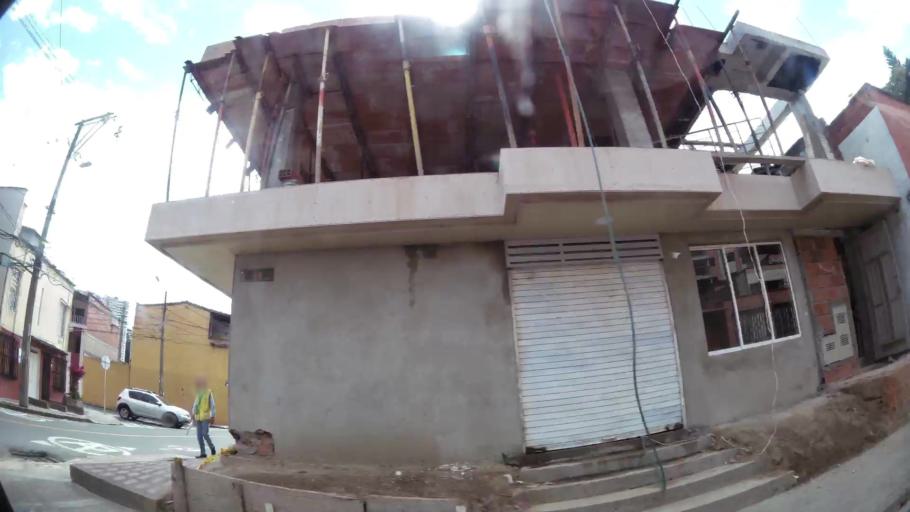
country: CO
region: Antioquia
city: Sabaneta
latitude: 6.1541
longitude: -75.6116
